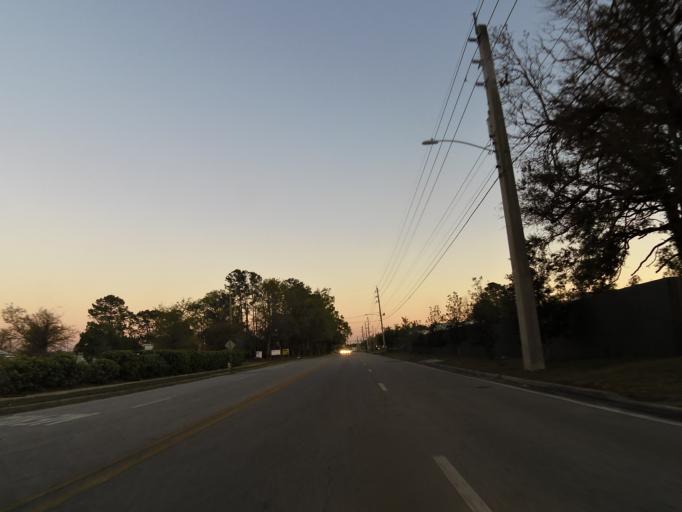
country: US
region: Florida
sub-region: Duval County
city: Jacksonville
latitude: 30.2661
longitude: -81.6238
